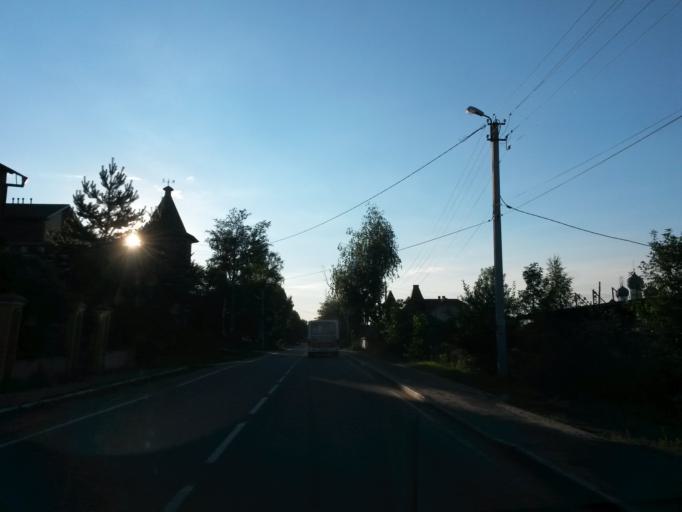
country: RU
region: Jaroslavl
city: Tutayev
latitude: 57.8715
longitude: 39.5291
